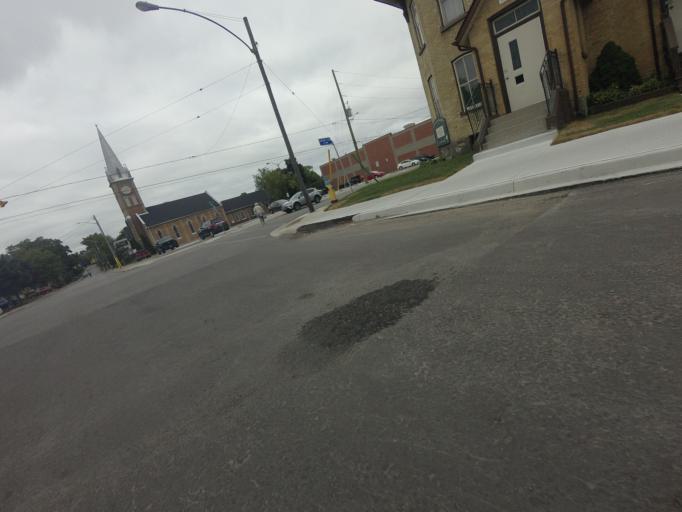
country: CA
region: Ontario
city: Omemee
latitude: 44.3556
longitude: -78.7398
